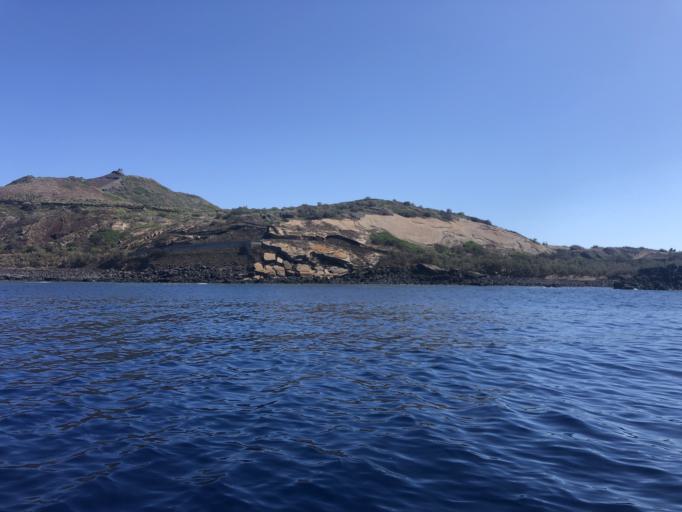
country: IT
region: Sicily
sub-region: Agrigento
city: Lampedusa
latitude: 35.8763
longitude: 12.8659
